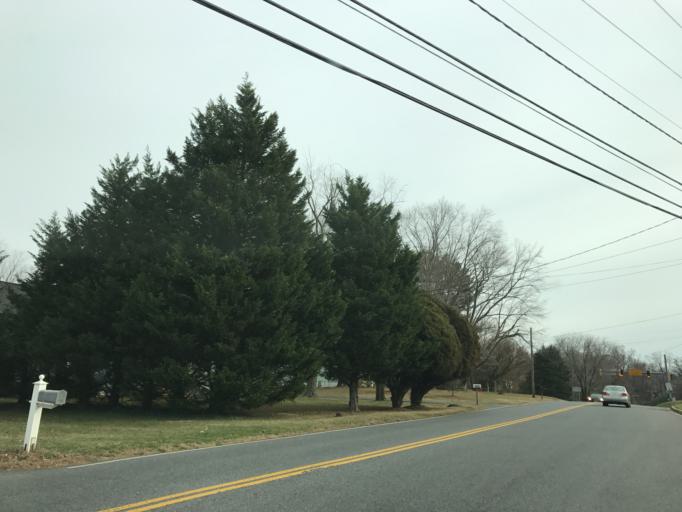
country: US
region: Maryland
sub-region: Anne Arundel County
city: Arnold
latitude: 39.0296
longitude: -76.5029
